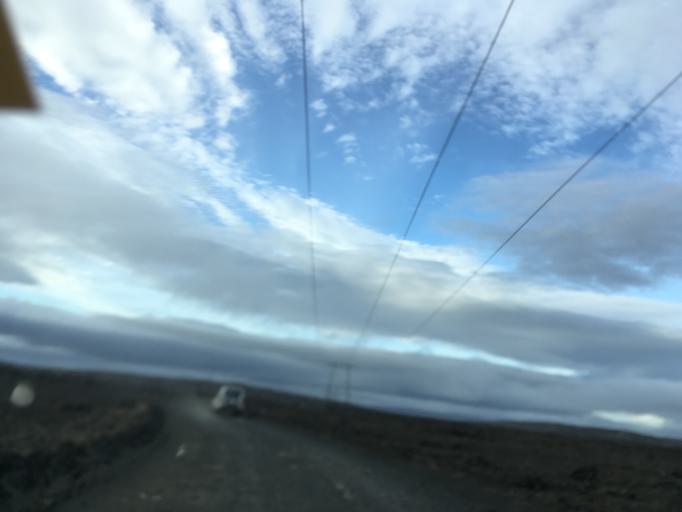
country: IS
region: South
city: Vestmannaeyjar
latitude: 64.1341
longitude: -19.1249
